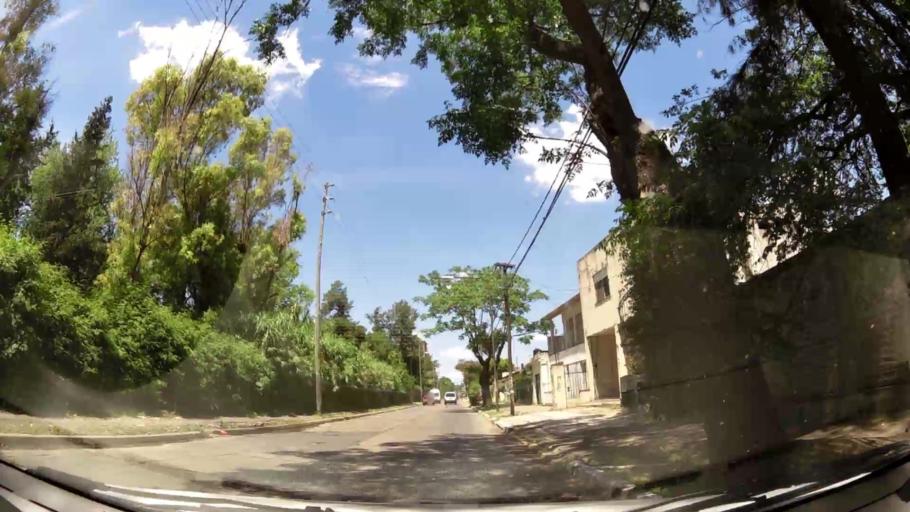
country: AR
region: Buenos Aires
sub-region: Partido de Merlo
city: Merlo
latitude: -34.6627
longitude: -58.7040
